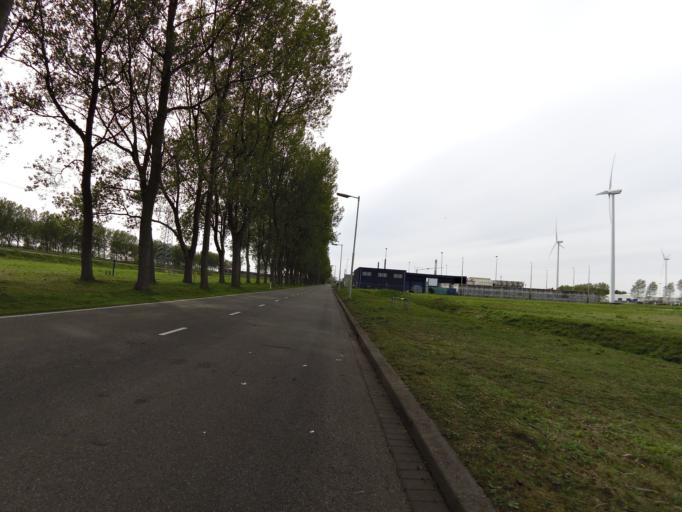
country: NL
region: South Holland
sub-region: Gemeente Rotterdam
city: Hoek van Holland
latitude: 51.9377
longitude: 4.1290
